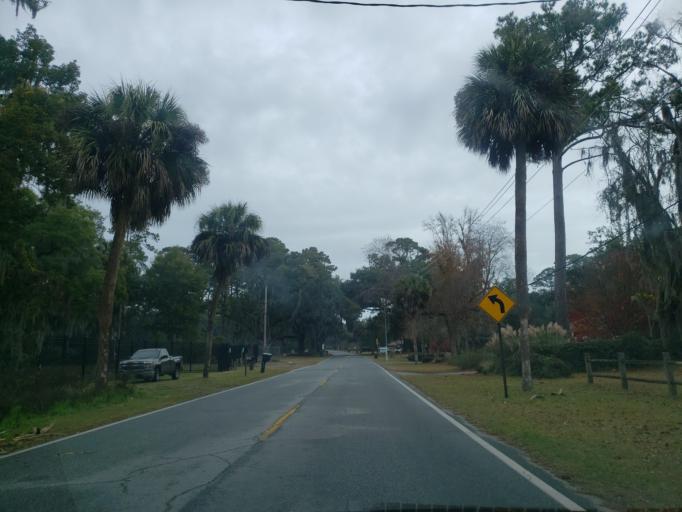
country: US
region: Georgia
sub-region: Chatham County
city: Wilmington Island
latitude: 31.9861
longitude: -80.9950
